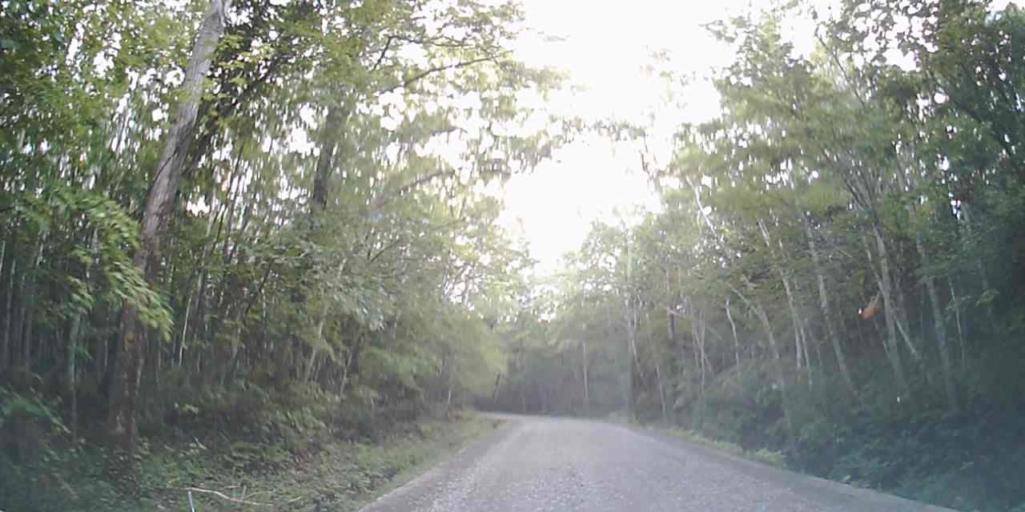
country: JP
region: Hokkaido
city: Shiraoi
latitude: 42.7171
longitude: 141.4069
